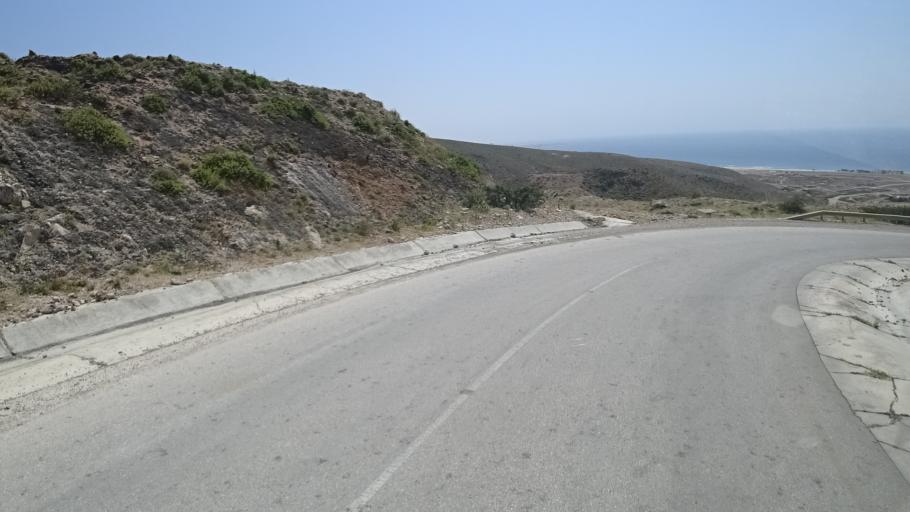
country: OM
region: Zufar
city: Salalah
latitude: 17.0484
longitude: 54.6131
